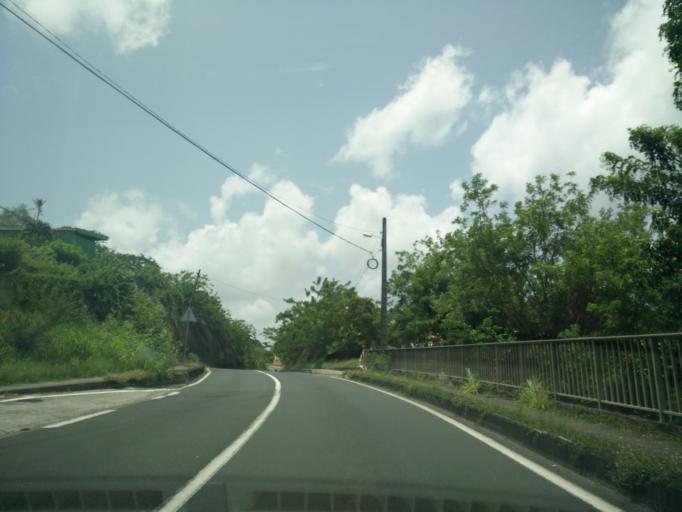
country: MQ
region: Martinique
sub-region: Martinique
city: Fort-de-France
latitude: 14.6241
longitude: -61.1097
